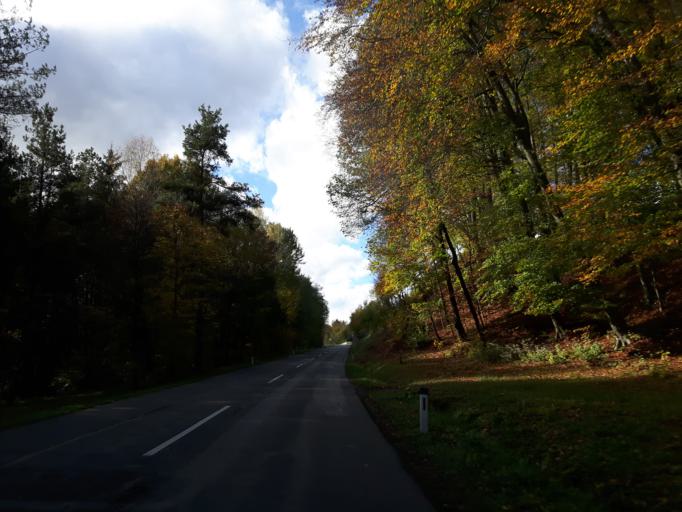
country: AT
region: Styria
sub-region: Politischer Bezirk Suedoststeiermark
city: Baumgarten bei Gnas
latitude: 46.9357
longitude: 15.7547
